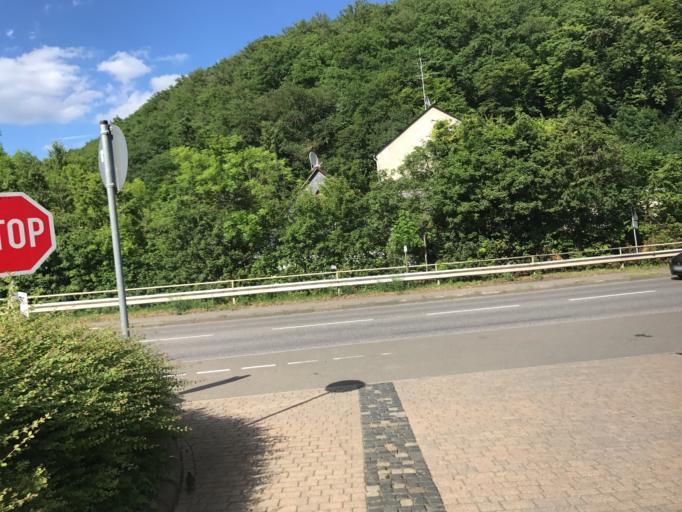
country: DE
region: Hesse
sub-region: Regierungsbezirk Darmstadt
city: Eltville
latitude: 50.0544
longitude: 8.1200
